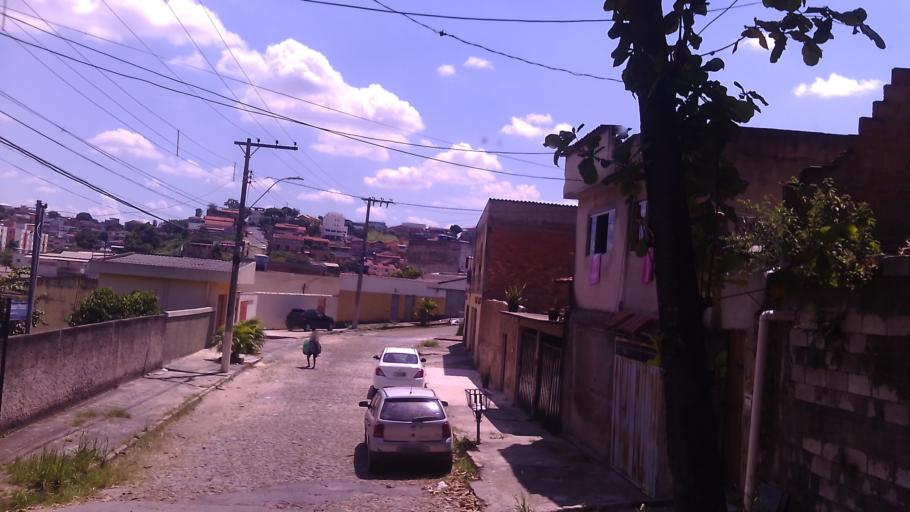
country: BR
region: Minas Gerais
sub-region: Belo Horizonte
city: Belo Horizonte
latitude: -19.8590
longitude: -43.9010
